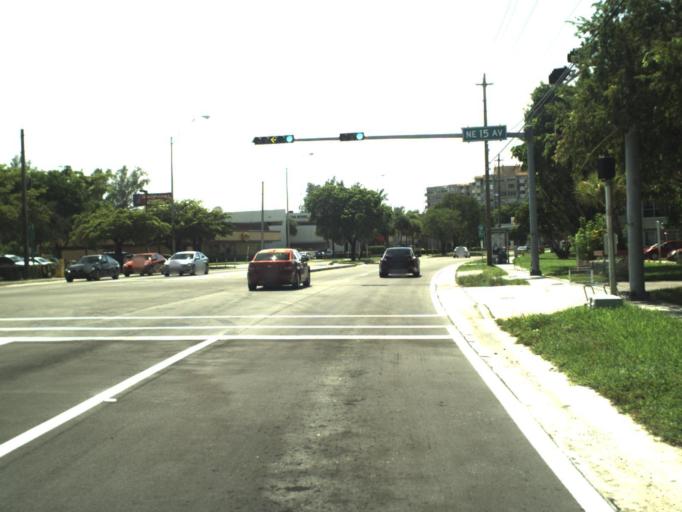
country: US
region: Florida
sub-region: Miami-Dade County
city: North Miami Beach
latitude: 25.9452
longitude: -80.1708
